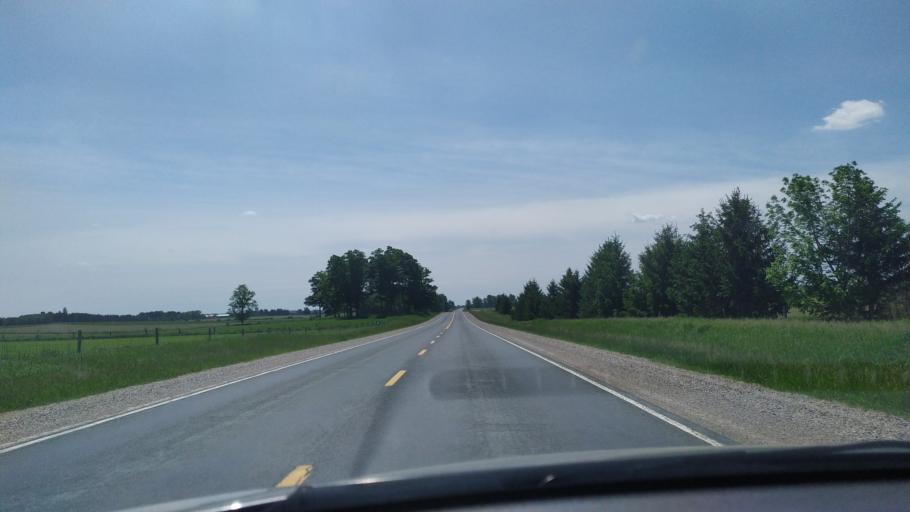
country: CA
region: Ontario
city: Ingersoll
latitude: 43.0346
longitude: -80.9752
